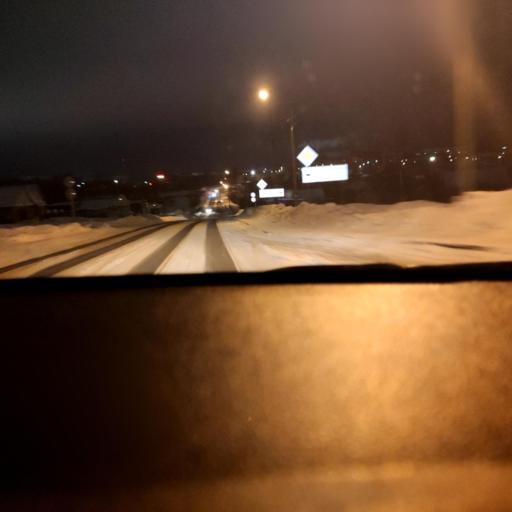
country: RU
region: Tatarstan
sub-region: Chistopol'skiy Rayon
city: Chistopol'
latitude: 55.3582
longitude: 50.6169
